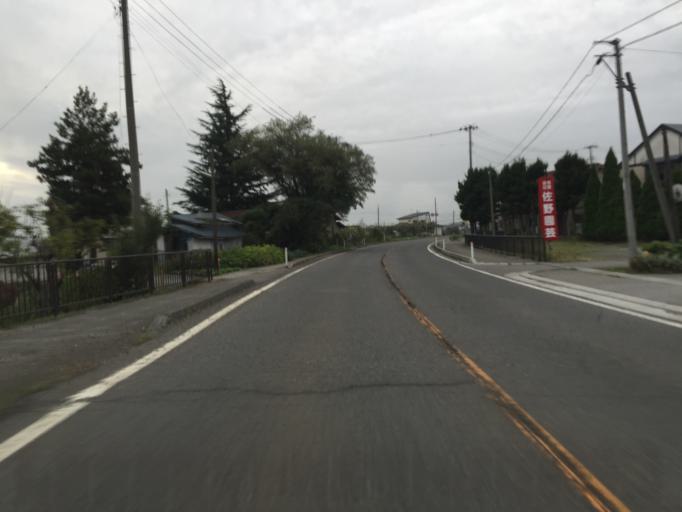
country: JP
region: Fukushima
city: Kitakata
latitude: 37.5516
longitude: 139.8686
